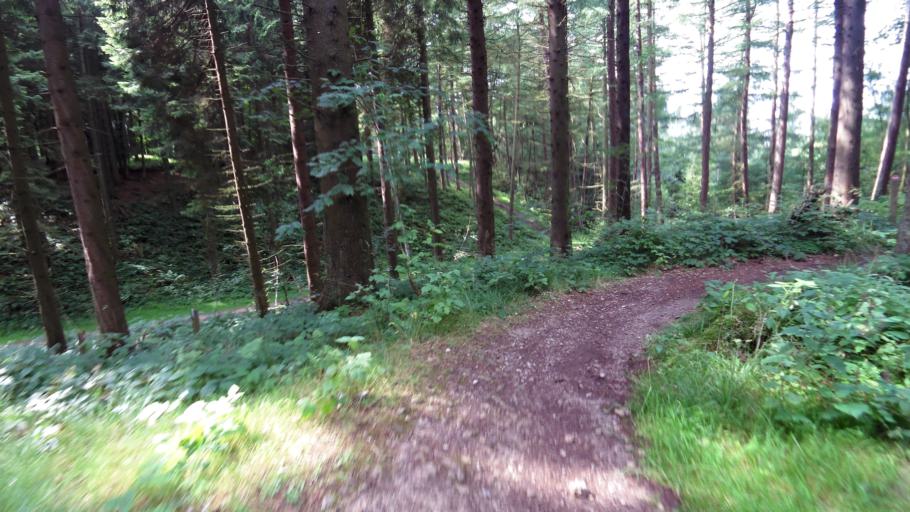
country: GB
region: England
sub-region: North Yorkshire
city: Thornton Dale
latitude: 54.2958
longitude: -0.6457
